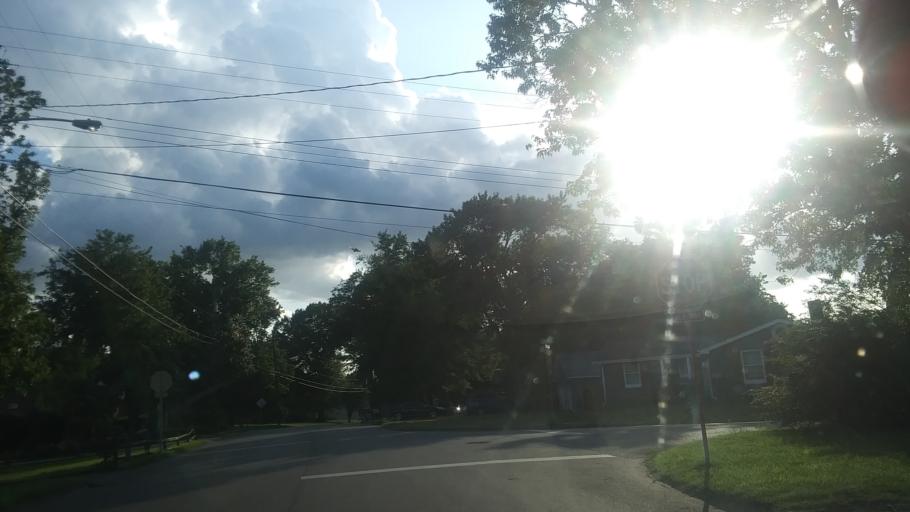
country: US
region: Tennessee
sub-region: Rutherford County
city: La Vergne
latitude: 36.0650
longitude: -86.6697
